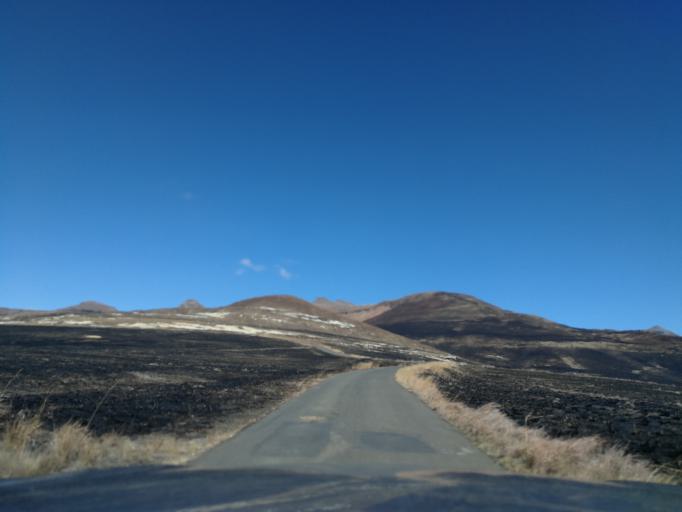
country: ZA
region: Orange Free State
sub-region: Thabo Mofutsanyana District Municipality
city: Phuthaditjhaba
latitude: -28.5178
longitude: 28.6226
